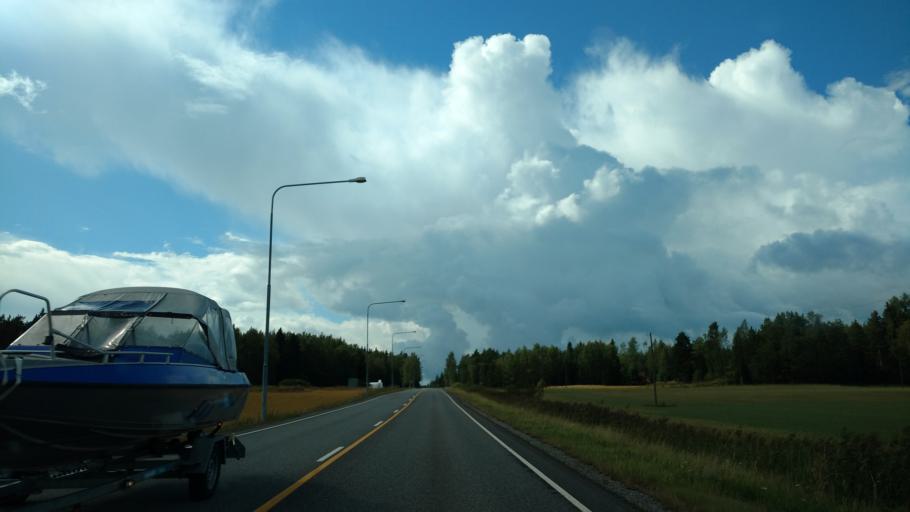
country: FI
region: Varsinais-Suomi
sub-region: Turku
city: Paimio
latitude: 60.4193
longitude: 22.7479
